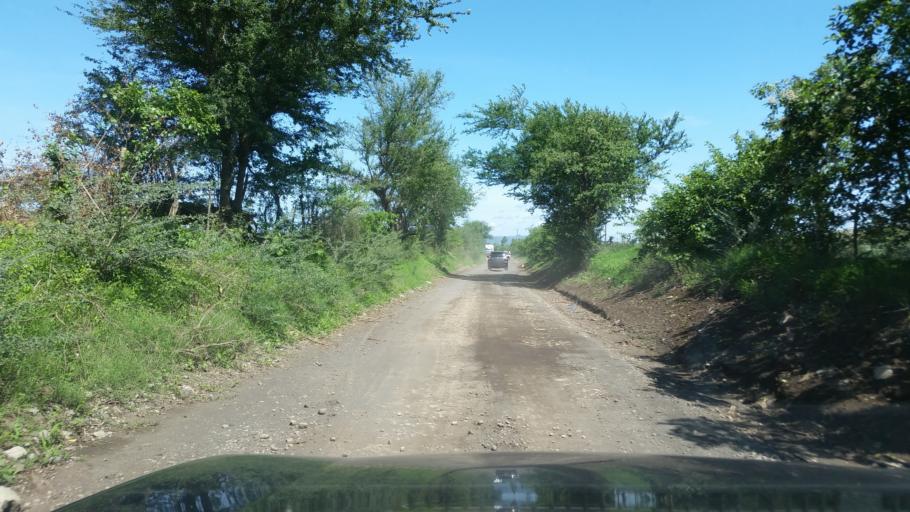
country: NI
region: Chinandega
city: Puerto Morazan
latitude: 12.7711
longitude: -87.0888
